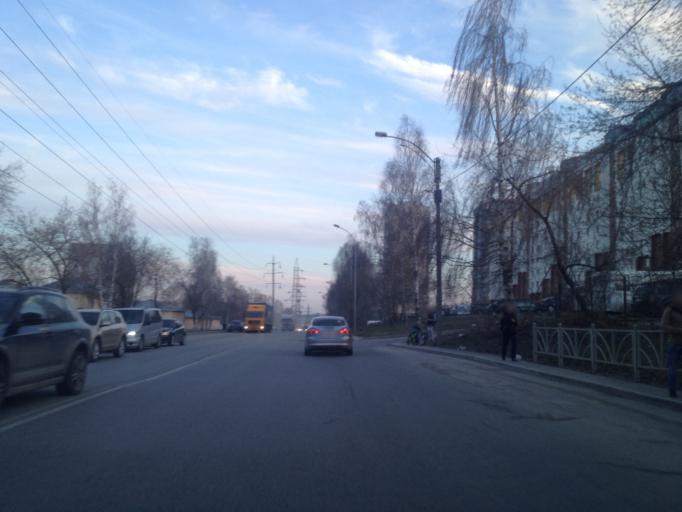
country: RU
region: Sverdlovsk
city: Sovkhoznyy
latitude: 56.7808
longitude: 60.5983
